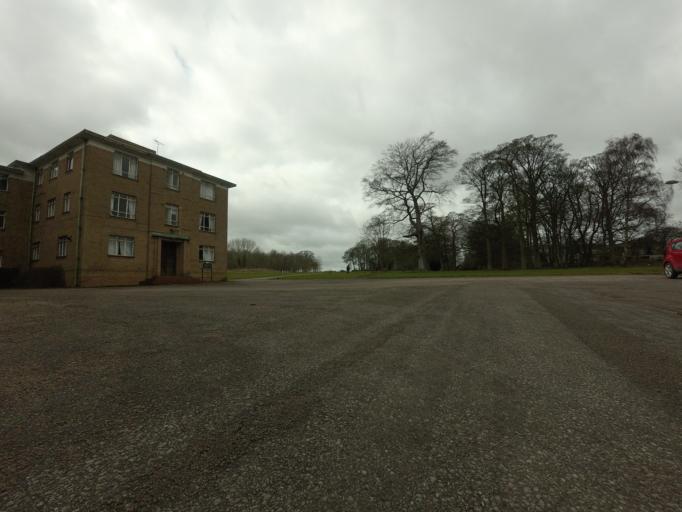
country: GB
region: England
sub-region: Lincolnshire
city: Grantham
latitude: 52.8417
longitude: -0.6426
